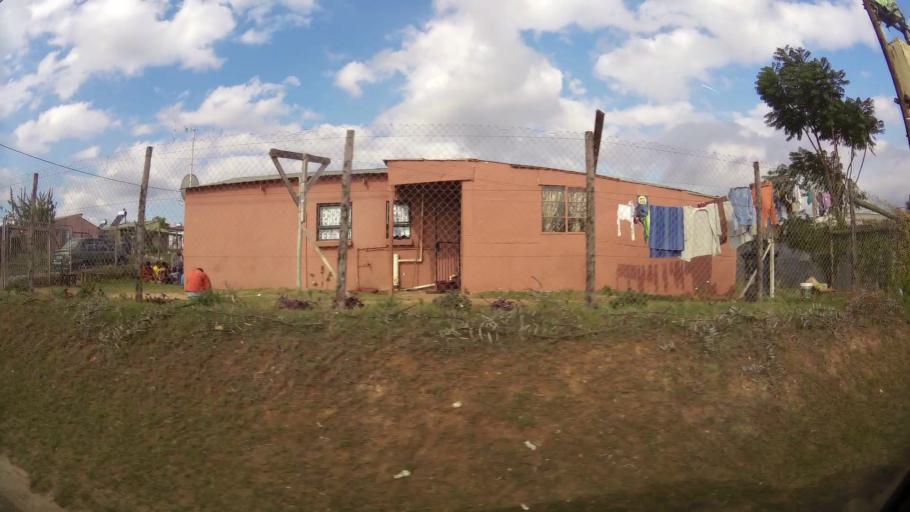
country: ZA
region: Eastern Cape
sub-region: Nelson Mandela Bay Metropolitan Municipality
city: Uitenhage
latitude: -33.7480
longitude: 25.3927
